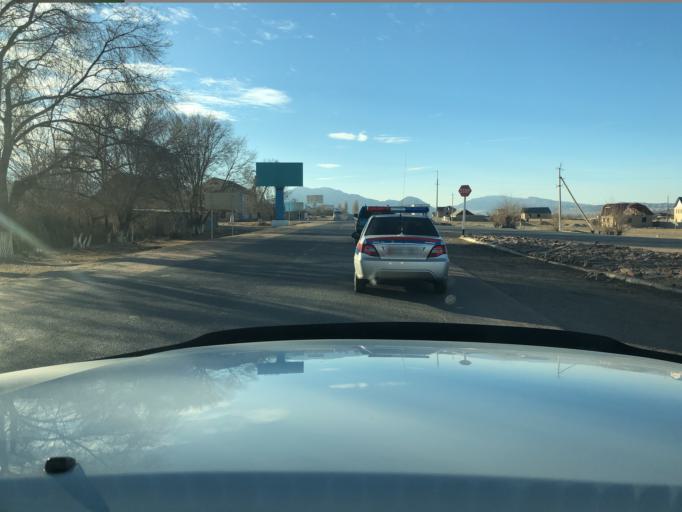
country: KG
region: Ysyk-Koel
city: Bokombayevskoye
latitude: 42.1155
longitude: 76.9812
